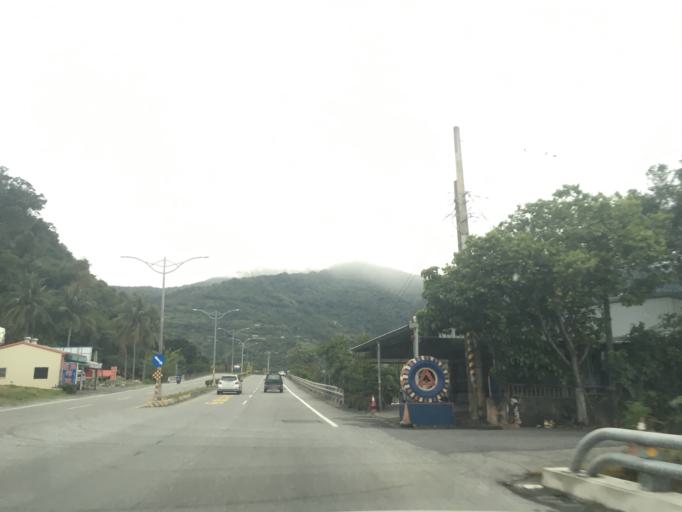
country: TW
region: Taiwan
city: Taitung City
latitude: 22.6990
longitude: 121.0417
